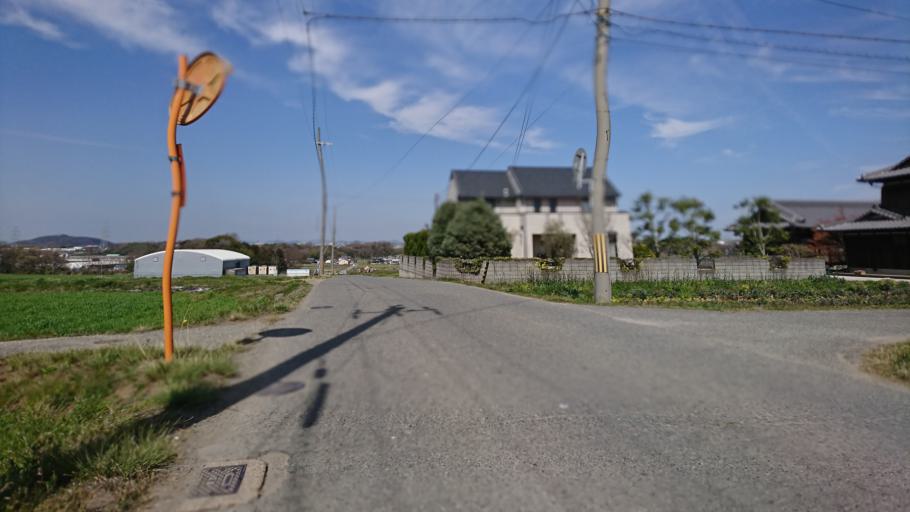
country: JP
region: Hyogo
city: Miki
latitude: 34.7691
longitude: 134.9342
